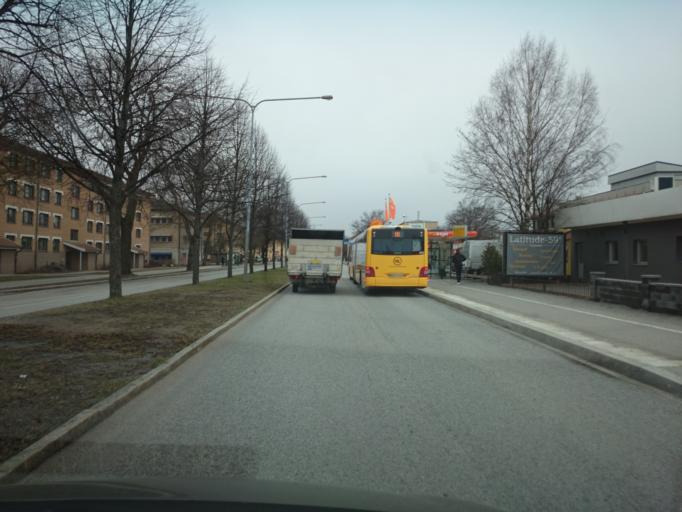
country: SE
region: Uppsala
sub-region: Uppsala Kommun
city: Uppsala
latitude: 59.8684
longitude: 17.6287
